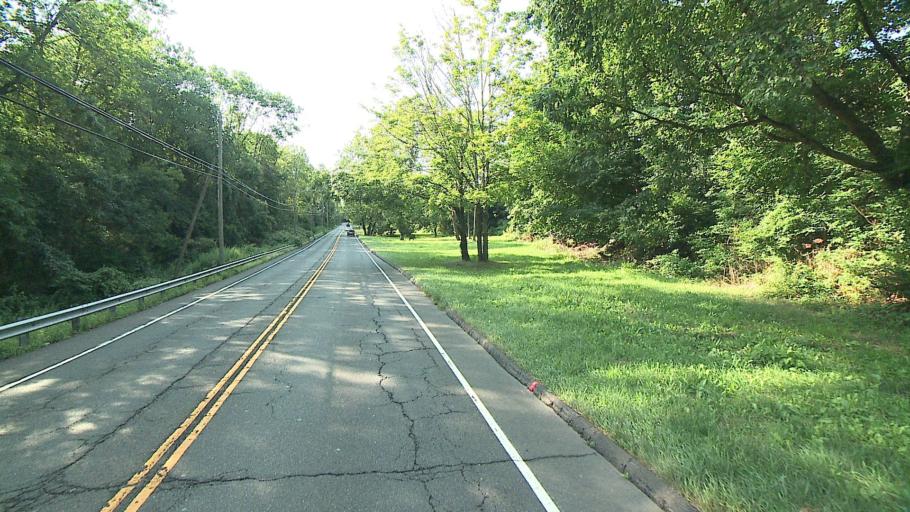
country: US
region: Connecticut
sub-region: Fairfield County
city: Georgetown
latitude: 41.2370
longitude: -73.4314
